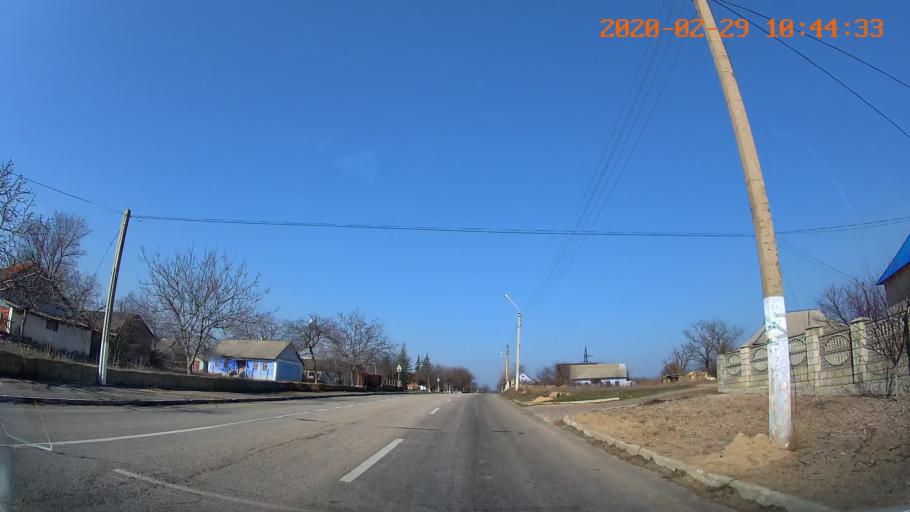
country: MD
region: Telenesti
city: Grigoriopol
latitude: 47.0708
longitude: 29.3935
